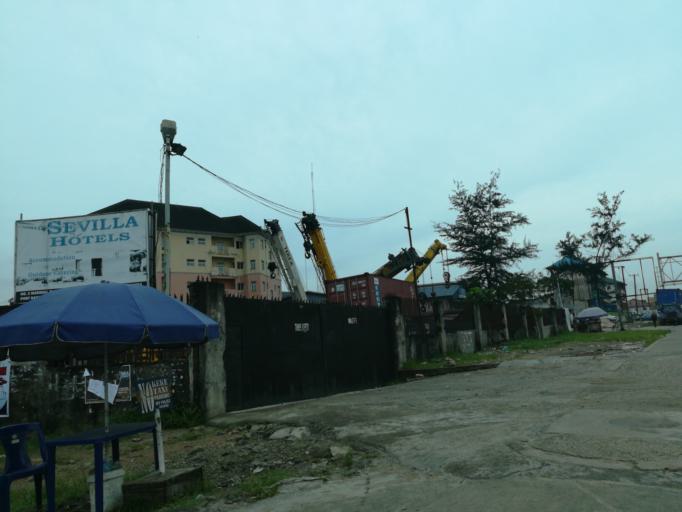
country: NG
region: Rivers
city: Port Harcourt
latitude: 4.8415
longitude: 7.0331
